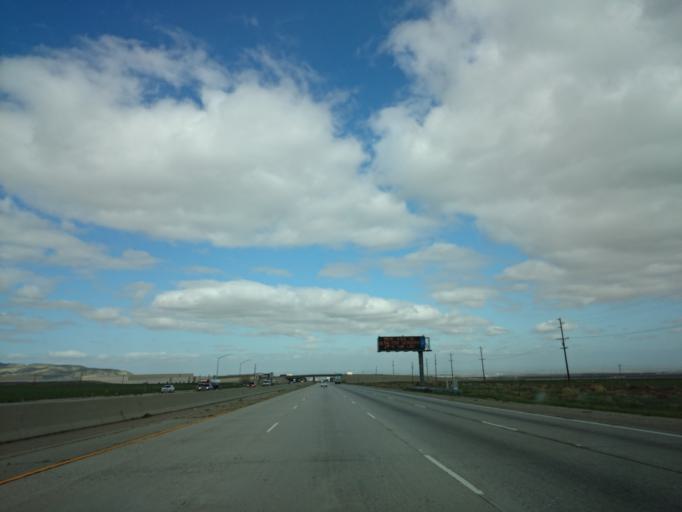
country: US
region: California
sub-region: Kern County
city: Frazier Park
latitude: 34.9671
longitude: -118.9391
